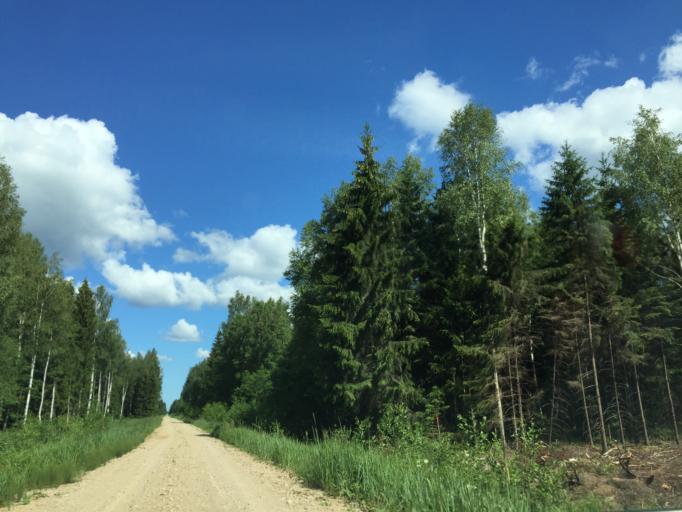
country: LV
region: Ventspils Rajons
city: Piltene
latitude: 57.2753
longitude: 21.8545
